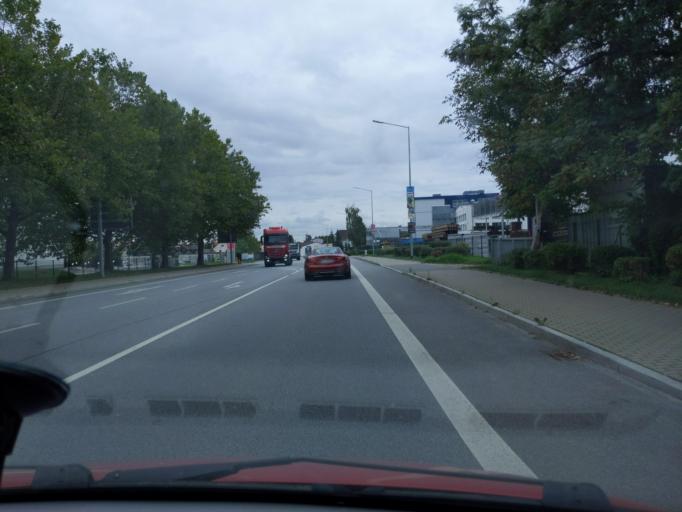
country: DE
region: Saxony
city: Bautzen
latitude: 51.1687
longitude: 14.4273
